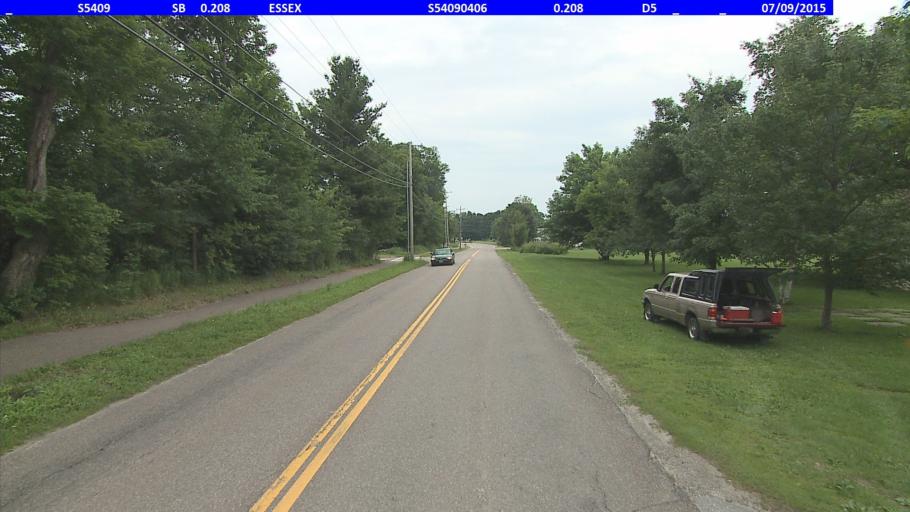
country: US
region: Vermont
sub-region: Chittenden County
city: Essex Junction
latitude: 44.5130
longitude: -73.0828
